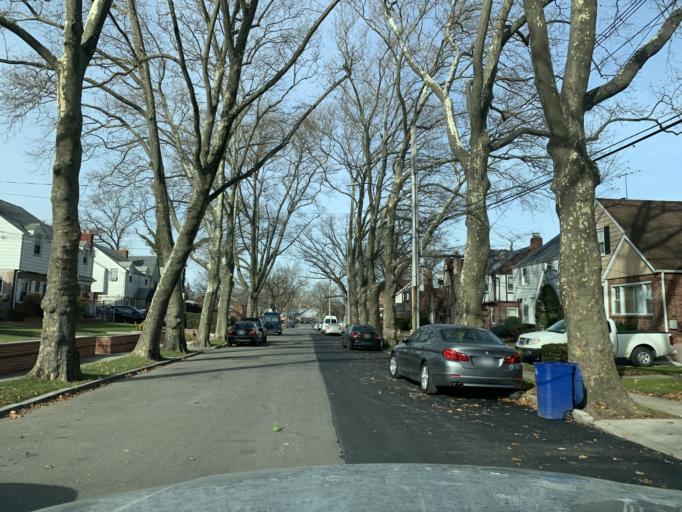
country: US
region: New York
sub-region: Queens County
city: Jamaica
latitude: 40.6963
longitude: -73.7717
